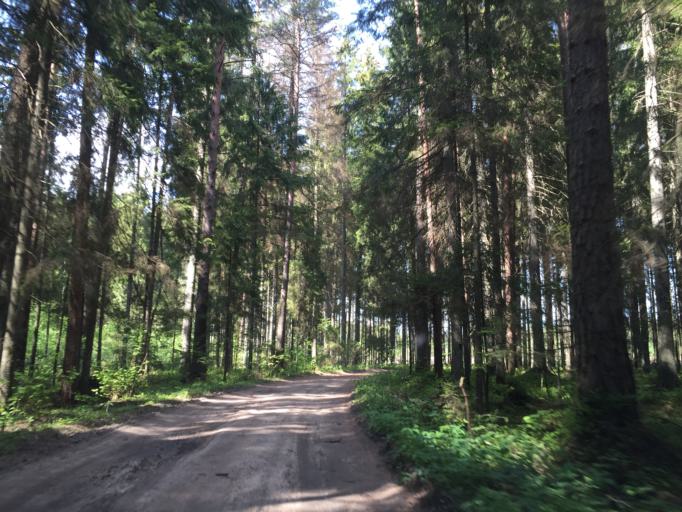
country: LV
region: Baldone
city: Baldone
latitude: 56.7838
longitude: 24.4217
